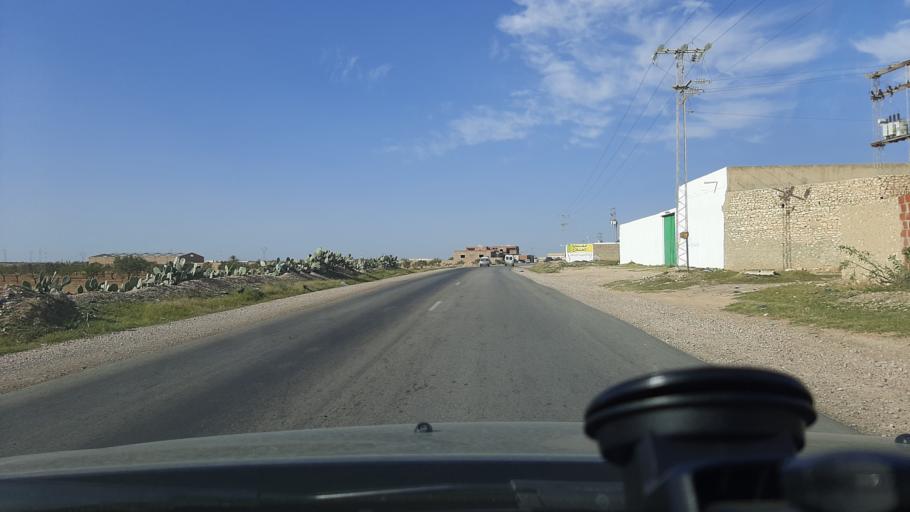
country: TN
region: Safaqis
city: Sfax
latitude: 34.7965
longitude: 10.6366
